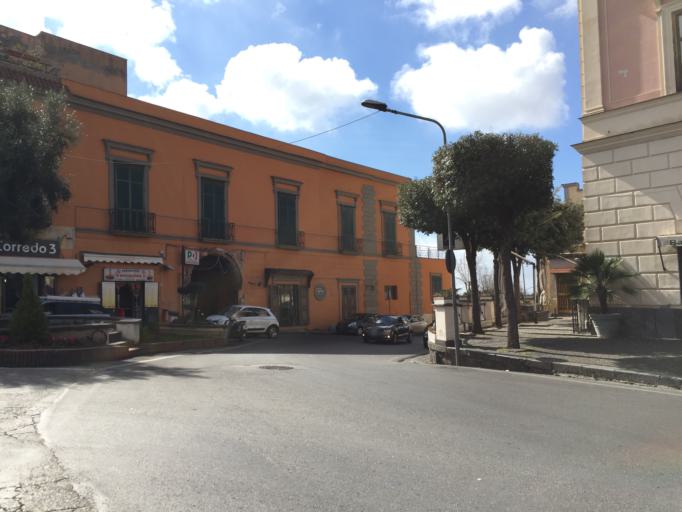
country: IT
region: Campania
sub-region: Provincia di Napoli
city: San Sebastiano al Vesuvio
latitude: 40.8431
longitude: 14.3698
